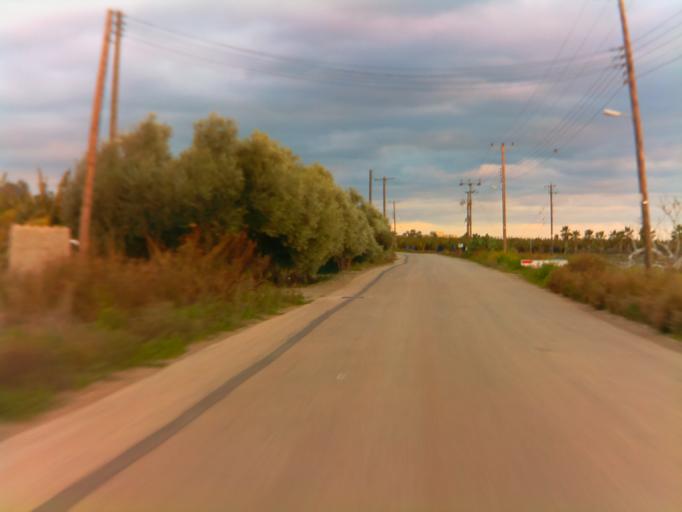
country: CY
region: Pafos
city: Pegeia
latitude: 34.8676
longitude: 32.3504
